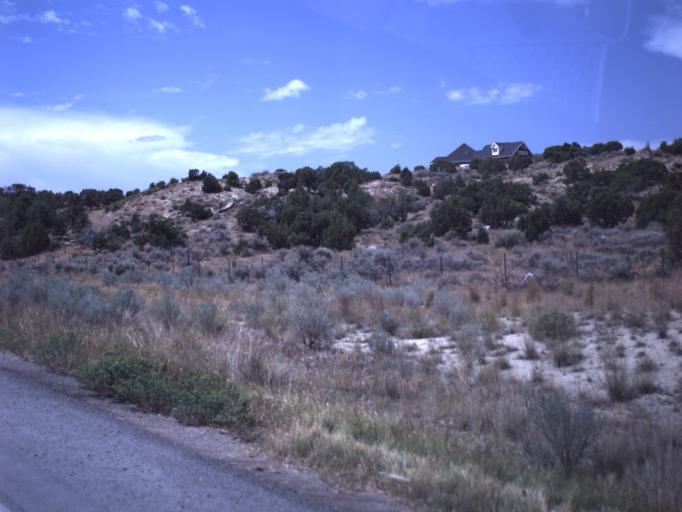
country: US
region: Utah
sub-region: Uintah County
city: Maeser
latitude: 40.4297
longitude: -109.5764
